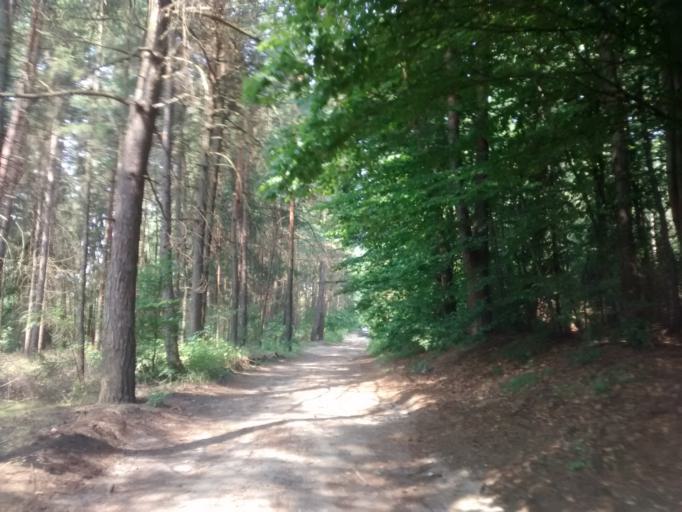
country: PL
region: Lesser Poland Voivodeship
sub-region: Powiat olkuski
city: Olkusz
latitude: 50.3032
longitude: 19.5841
